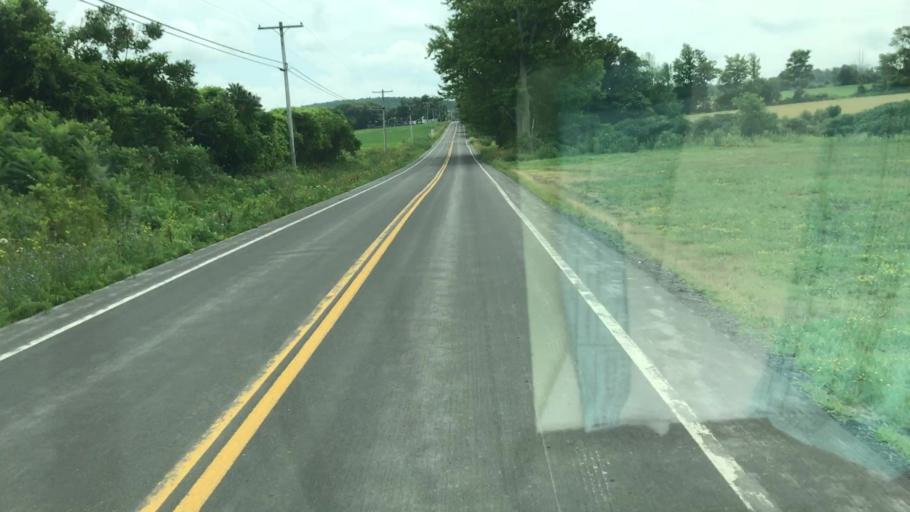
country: US
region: New York
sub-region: Onondaga County
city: Manlius
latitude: 42.9296
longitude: -75.9765
